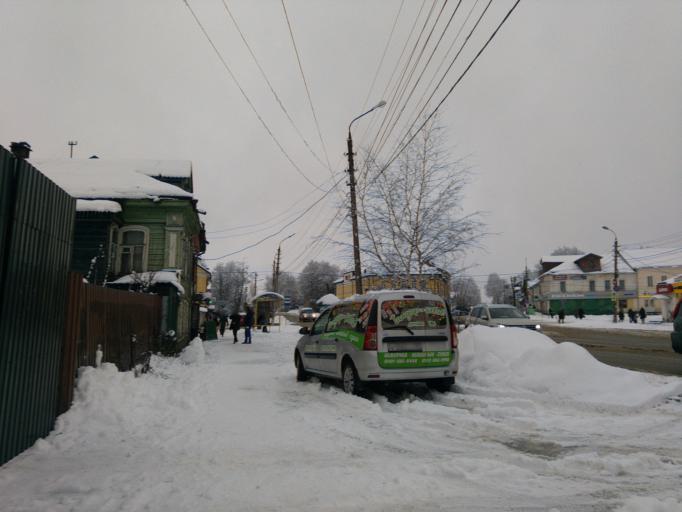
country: RU
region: Tverskaya
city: Torzhok
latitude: 57.0441
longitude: 34.9689
